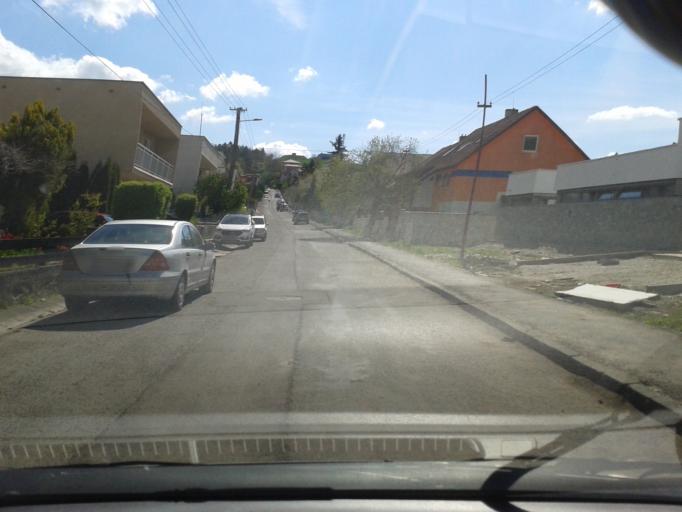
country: SK
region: Banskobystricky
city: Dudince
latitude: 48.1669
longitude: 18.8919
